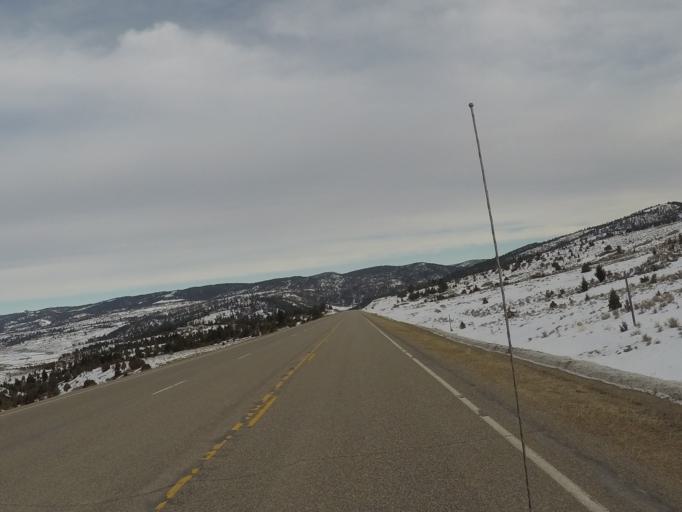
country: US
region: Montana
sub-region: Meagher County
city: White Sulphur Springs
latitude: 46.6527
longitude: -110.8714
